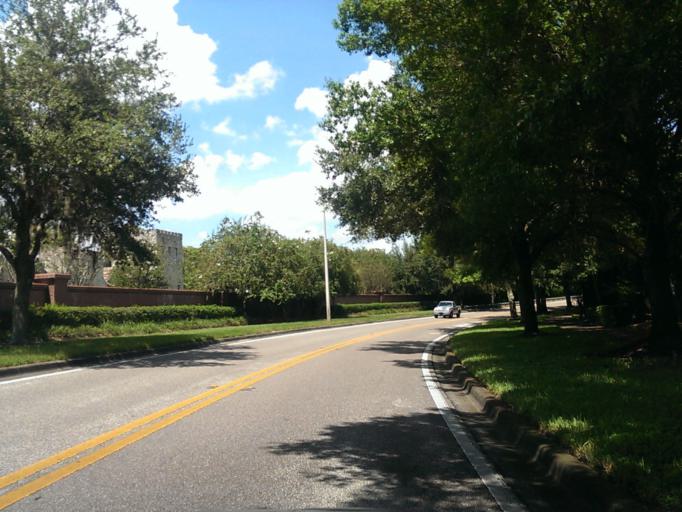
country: US
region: Florida
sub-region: Orange County
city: Windermere
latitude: 28.4770
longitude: -81.5444
